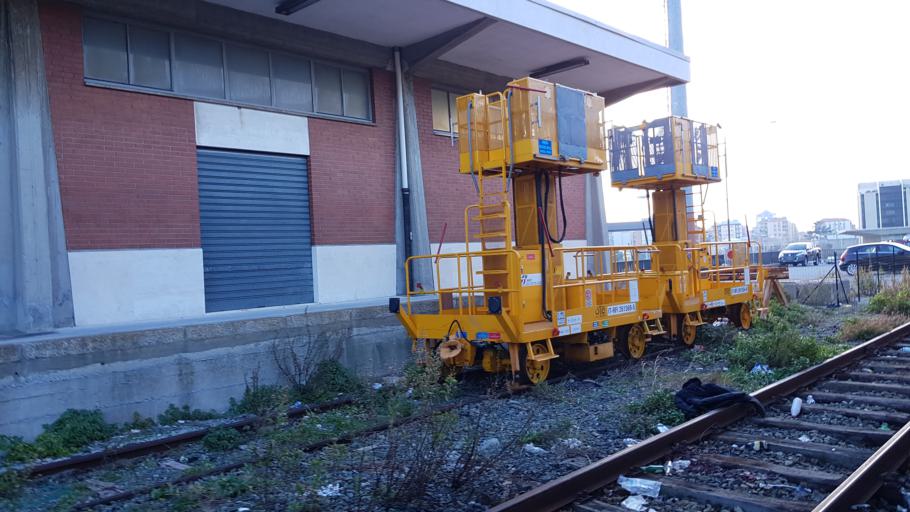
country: IT
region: Liguria
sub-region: Provincia di Savona
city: Savona
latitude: 44.3092
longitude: 8.4708
